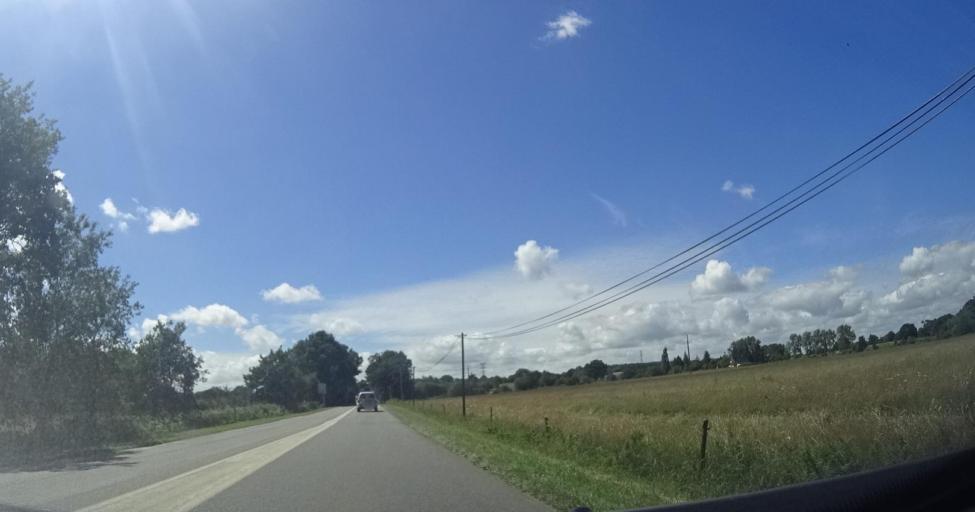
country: FR
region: Brittany
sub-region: Departement du Morbihan
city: Questembert
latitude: 47.6874
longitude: -2.4619
